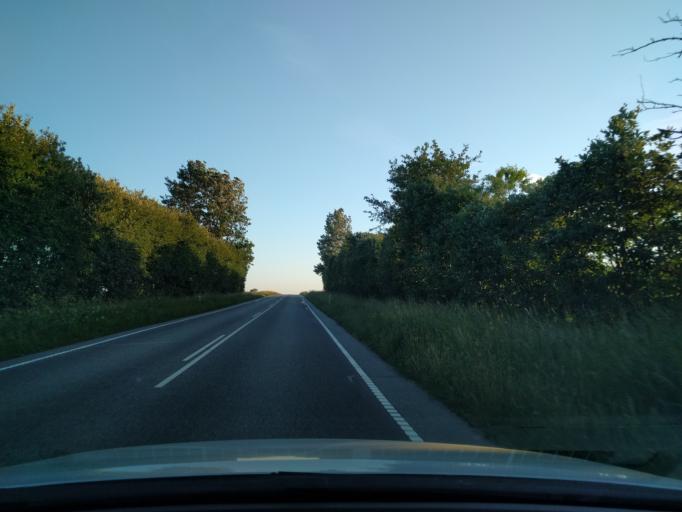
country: DK
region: South Denmark
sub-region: Kerteminde Kommune
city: Kerteminde
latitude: 55.4850
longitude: 10.6238
